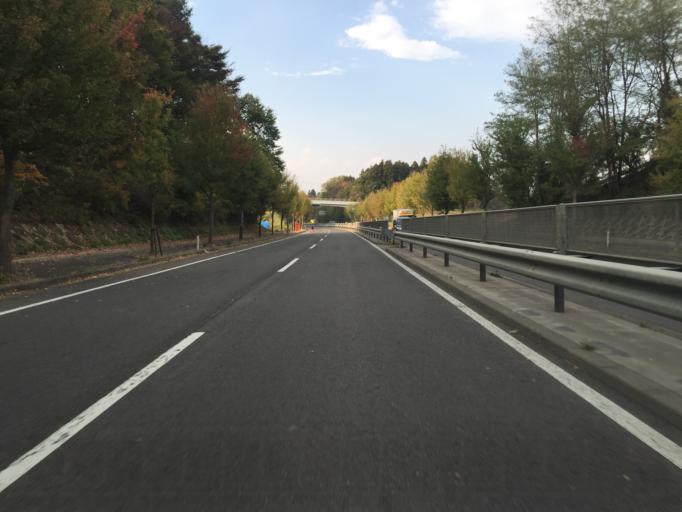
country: JP
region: Fukushima
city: Fukushima-shi
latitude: 37.6641
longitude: 140.4891
